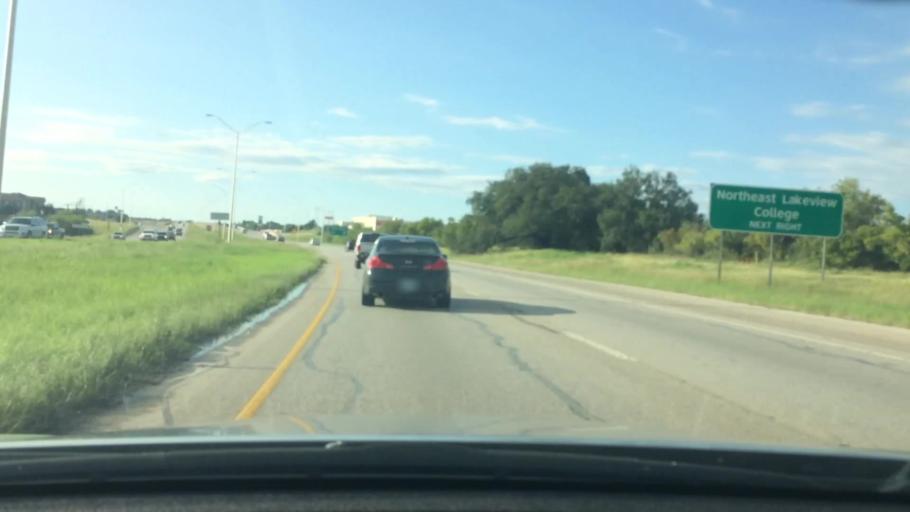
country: US
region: Texas
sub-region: Bexar County
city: Universal City
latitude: 29.5423
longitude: -98.3082
